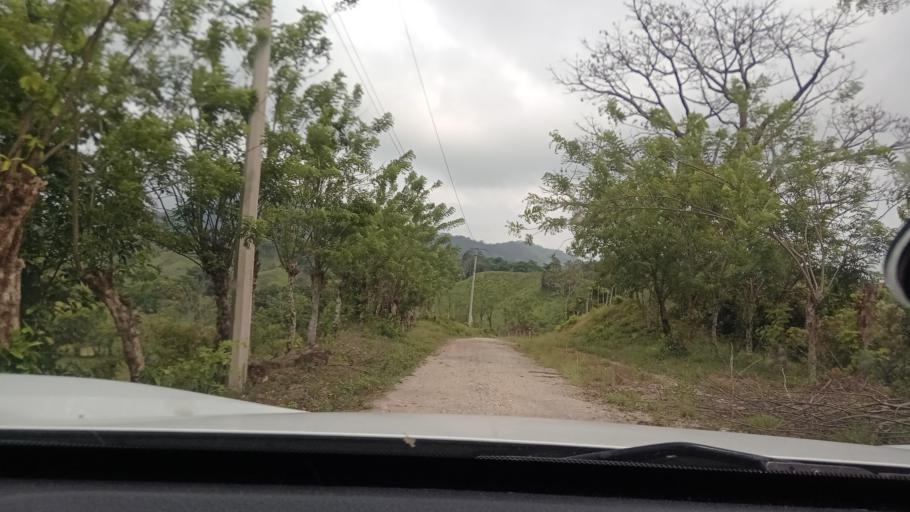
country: MX
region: Tabasco
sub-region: Huimanguillo
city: Francisco Rueda
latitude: 17.5222
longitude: -94.1257
